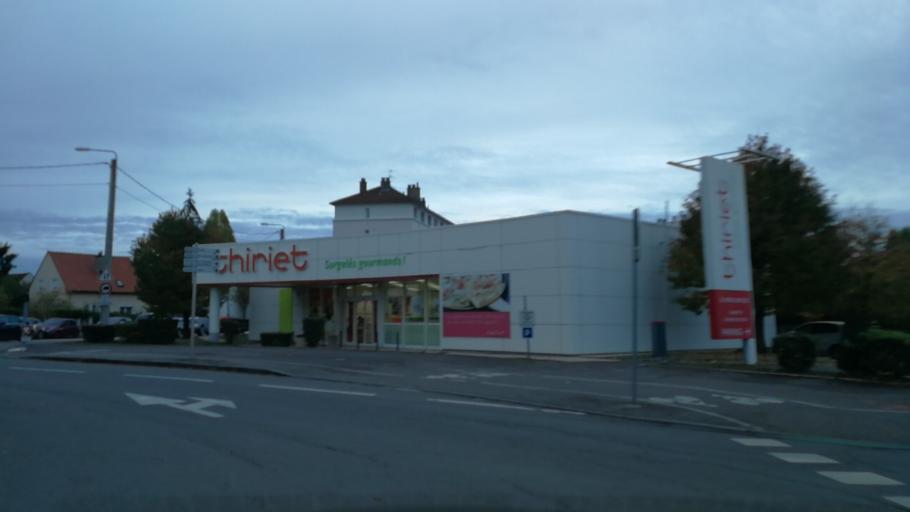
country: FR
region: Bourgogne
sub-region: Departement de la Cote-d'Or
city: Saint-Apollinaire
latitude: 47.3364
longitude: 5.0561
